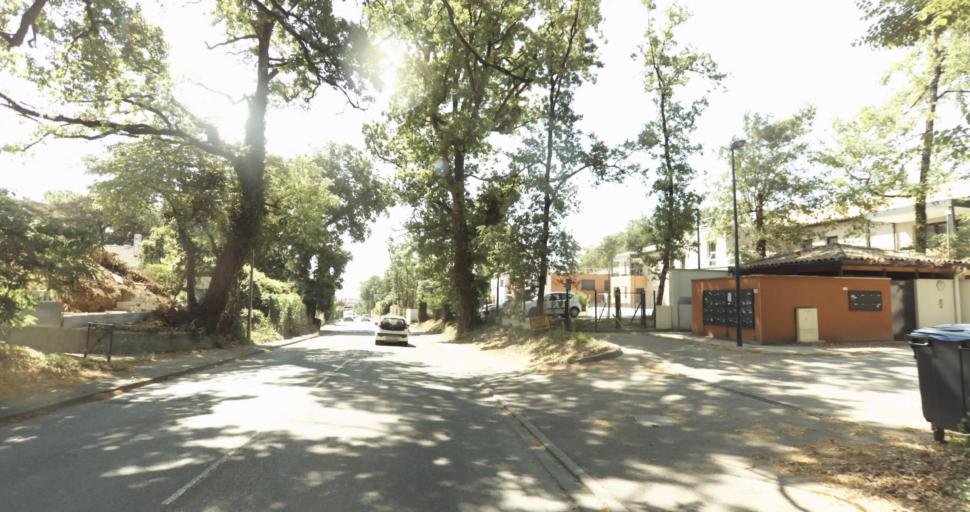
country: FR
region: Midi-Pyrenees
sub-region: Departement de la Haute-Garonne
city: Plaisance-du-Touch
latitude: 43.5731
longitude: 1.2920
